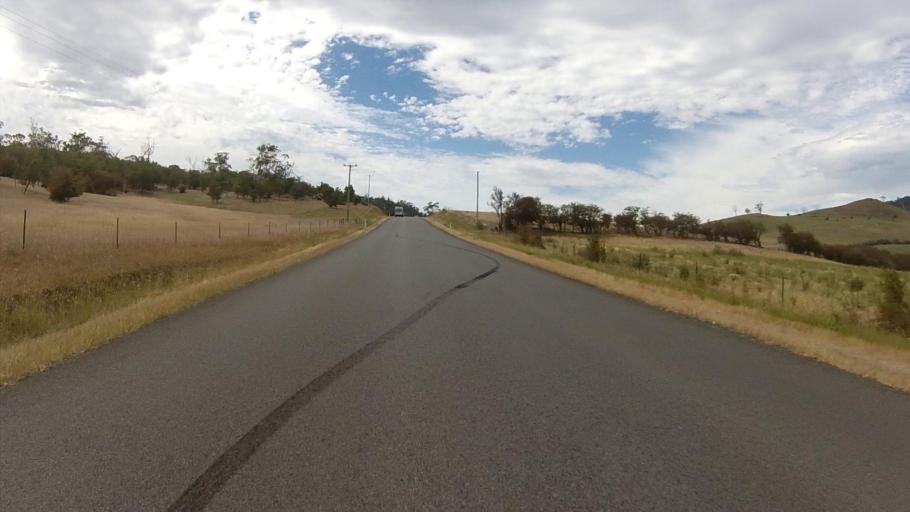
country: AU
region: Tasmania
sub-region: Brighton
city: Old Beach
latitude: -42.7194
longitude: 147.3321
